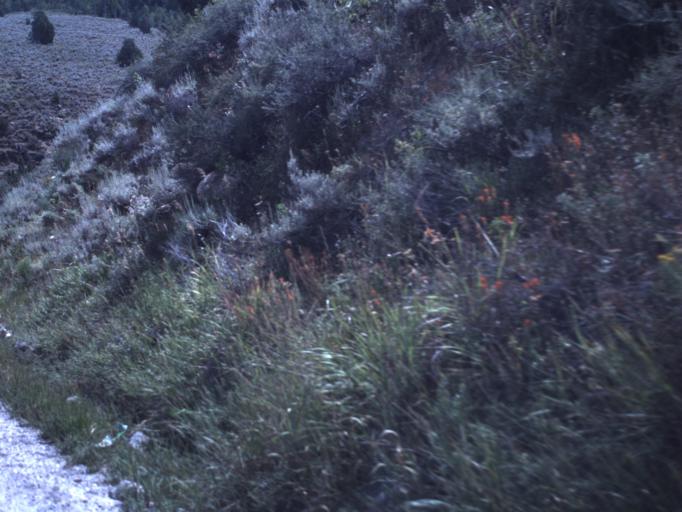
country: US
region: Utah
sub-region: Cache County
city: North Logan
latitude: 41.8427
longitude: -111.5860
